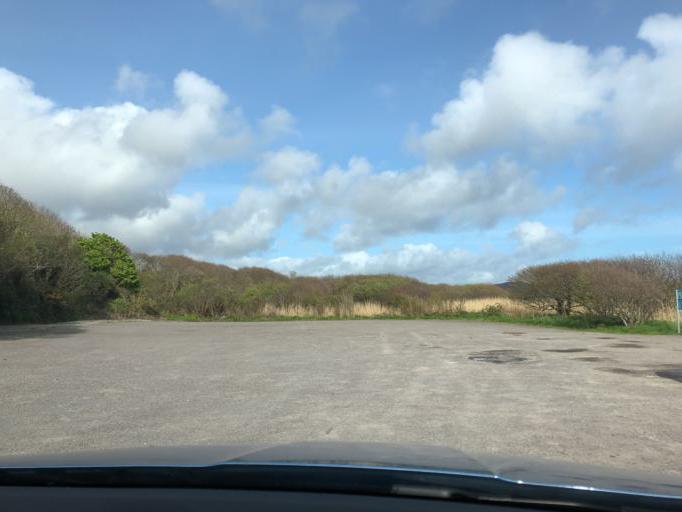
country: IE
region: Munster
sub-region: Ciarrai
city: Cahersiveen
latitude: 51.7606
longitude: -10.1373
